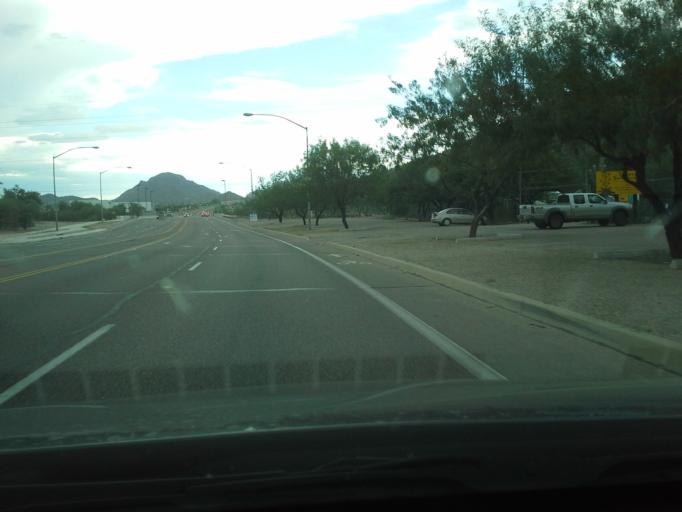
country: US
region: Arizona
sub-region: Pima County
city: South Tucson
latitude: 32.2069
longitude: -110.9866
